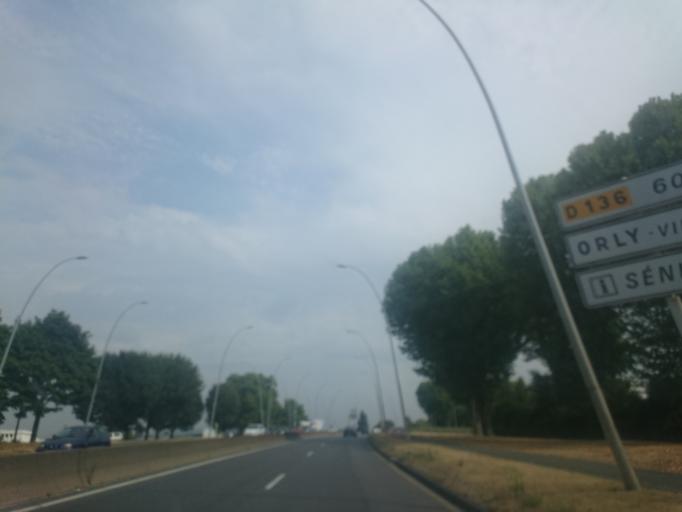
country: FR
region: Ile-de-France
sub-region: Departement du Val-de-Marne
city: Rungis
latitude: 48.7431
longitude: 2.3641
